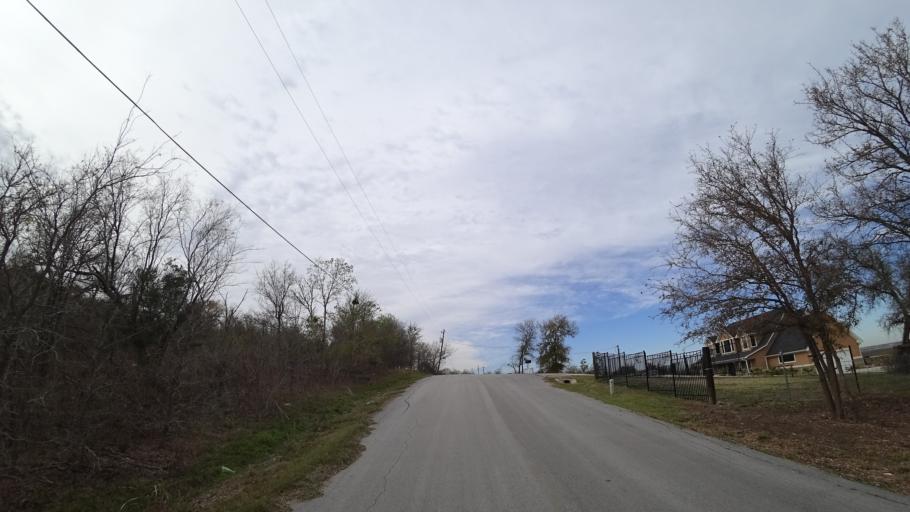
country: US
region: Texas
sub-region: Travis County
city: Garfield
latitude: 30.1470
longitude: -97.5869
